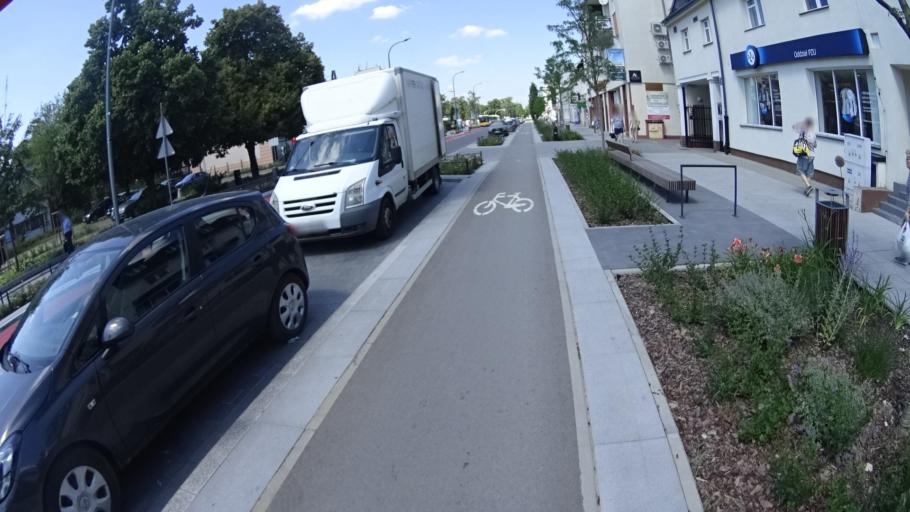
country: PL
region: Masovian Voivodeship
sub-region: Powiat piaseczynski
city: Piaseczno
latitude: 52.0759
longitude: 21.0269
